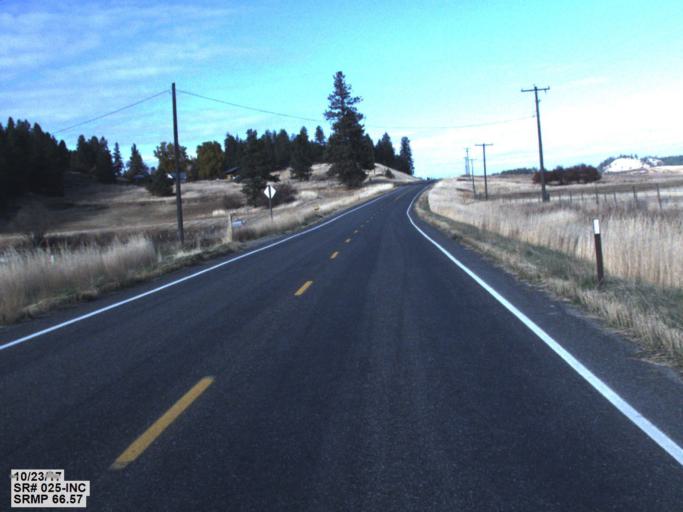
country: US
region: Washington
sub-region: Stevens County
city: Kettle Falls
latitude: 48.4322
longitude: -118.1709
